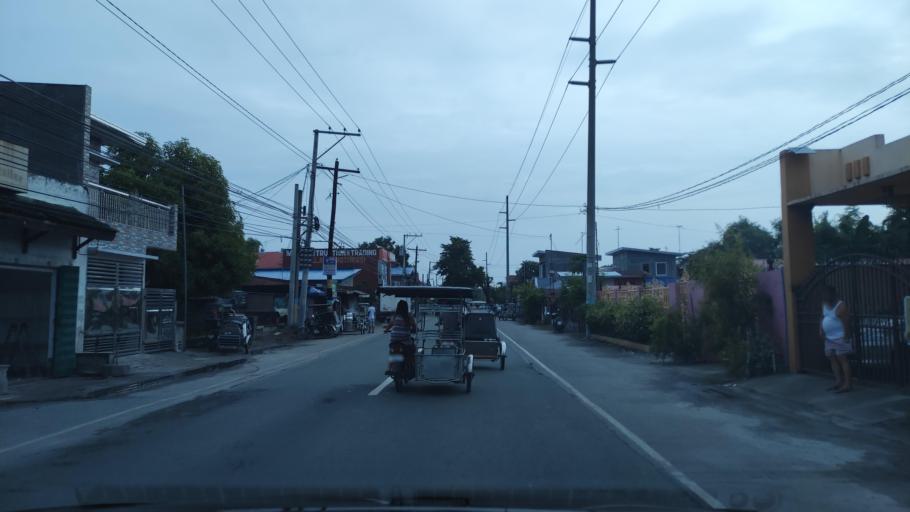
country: PH
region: Central Luzon
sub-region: Province of Pampanga
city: Santa Ana
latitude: 15.1098
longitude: 120.7720
